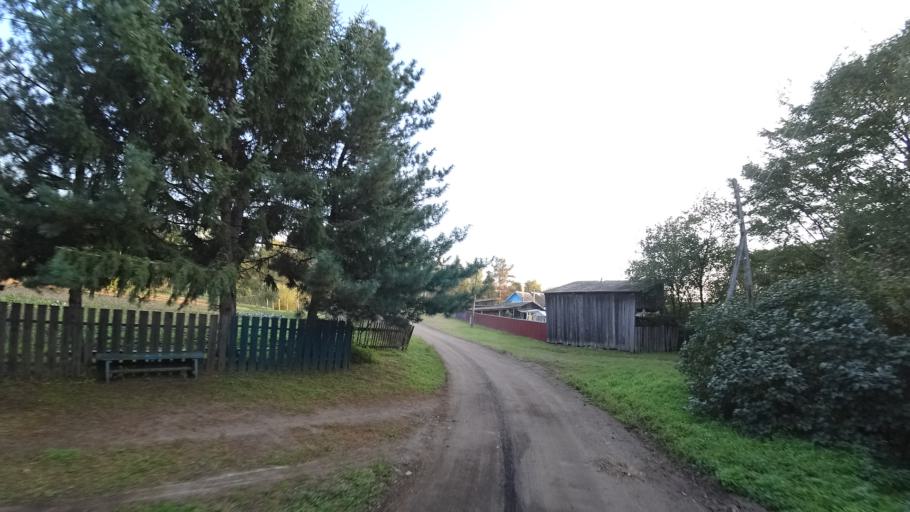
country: RU
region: Amur
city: Arkhara
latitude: 49.3631
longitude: 130.1173
